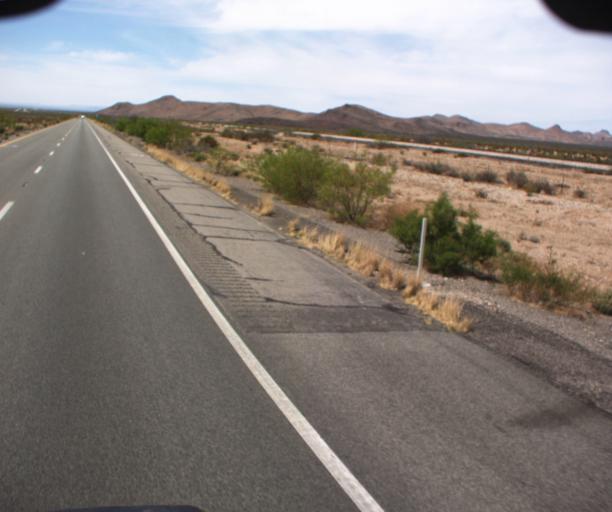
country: US
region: New Mexico
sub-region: Hidalgo County
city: Lordsburg
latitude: 32.2314
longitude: -109.0613
